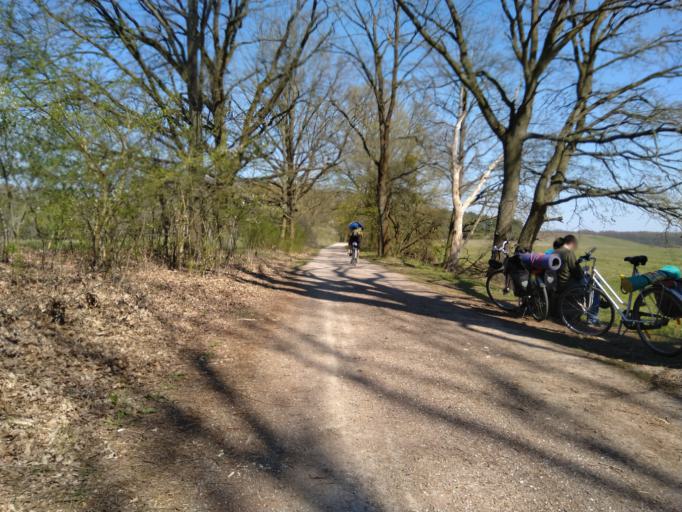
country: DE
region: Brandenburg
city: Biesenthal
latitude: 52.7542
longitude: 13.6249
